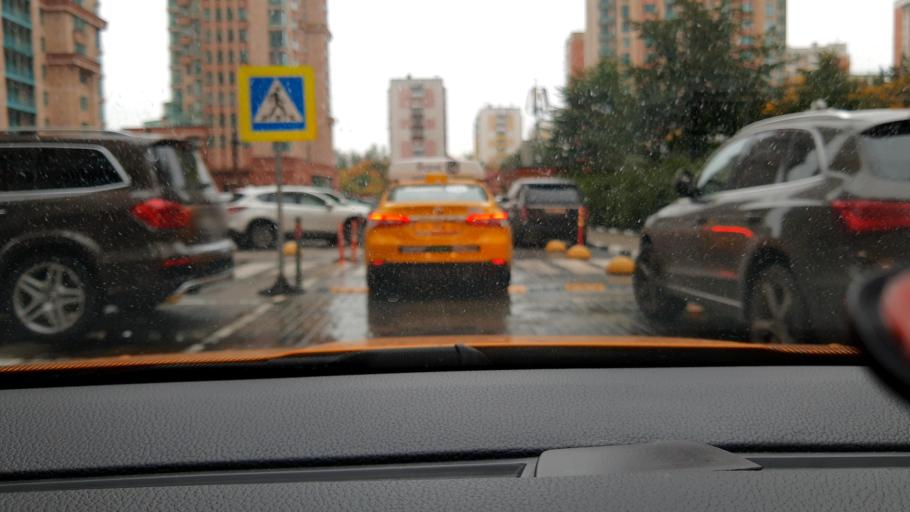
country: RU
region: Moscow
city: Shchukino
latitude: 55.8078
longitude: 37.4494
